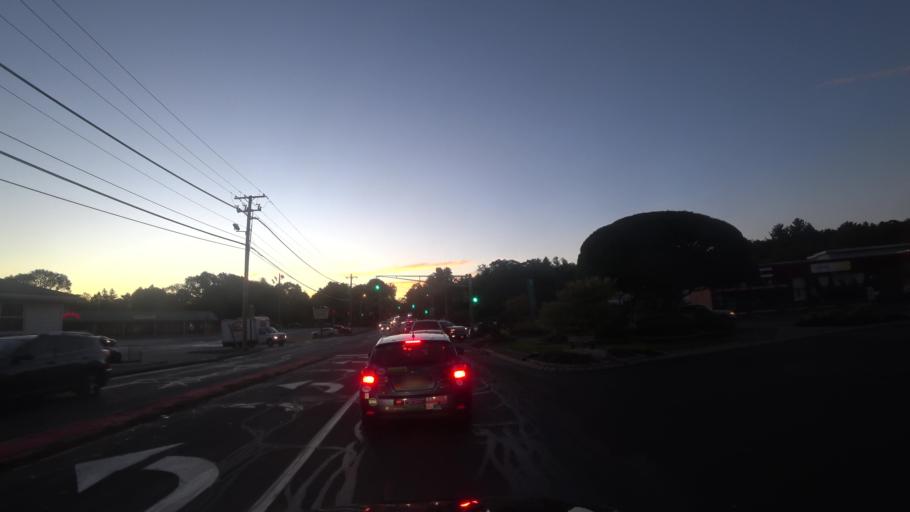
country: US
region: Massachusetts
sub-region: Essex County
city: Saugus
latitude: 42.4729
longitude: -71.0368
